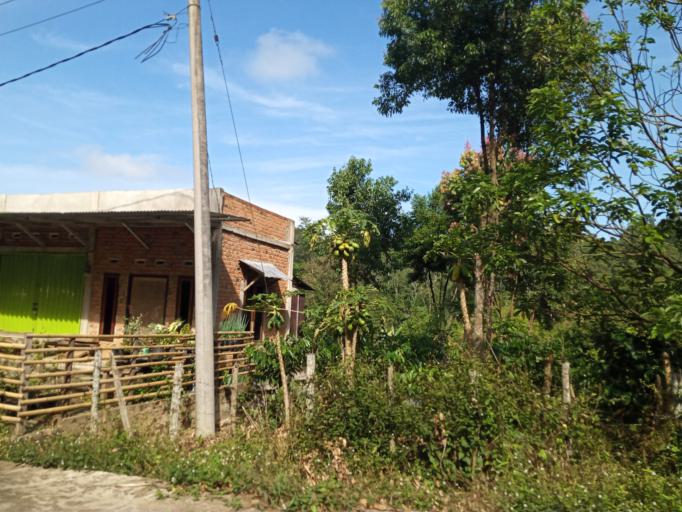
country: ID
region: Jambi
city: Sungai Penuh
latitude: -2.1497
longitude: 101.5668
